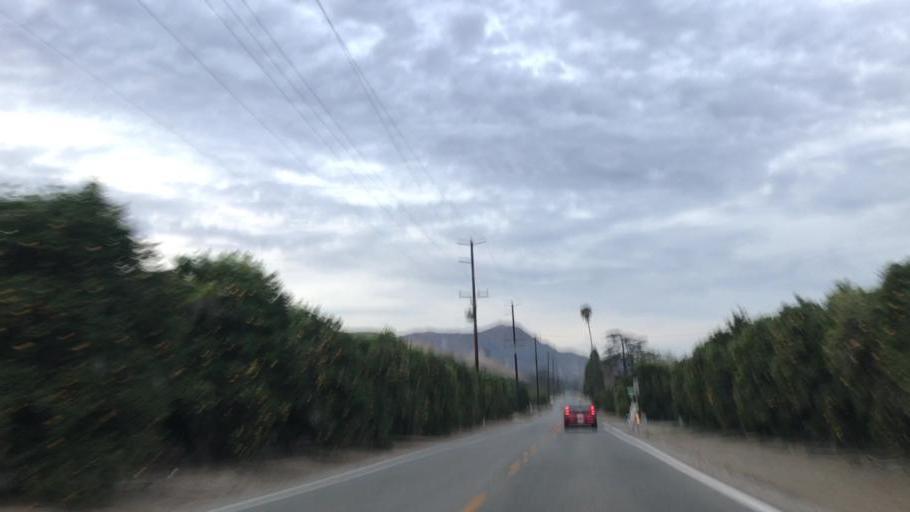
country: US
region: California
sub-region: Ventura County
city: Fillmore
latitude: 34.3618
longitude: -118.9501
